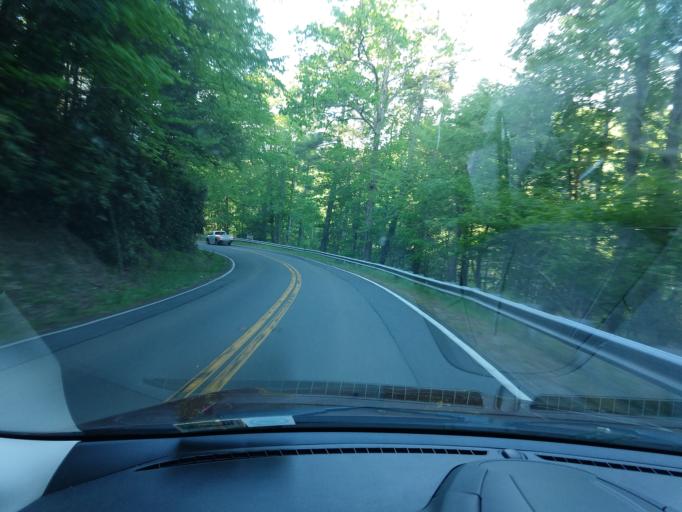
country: US
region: Virginia
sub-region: City of Galax
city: Galax
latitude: 36.7193
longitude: -80.9840
